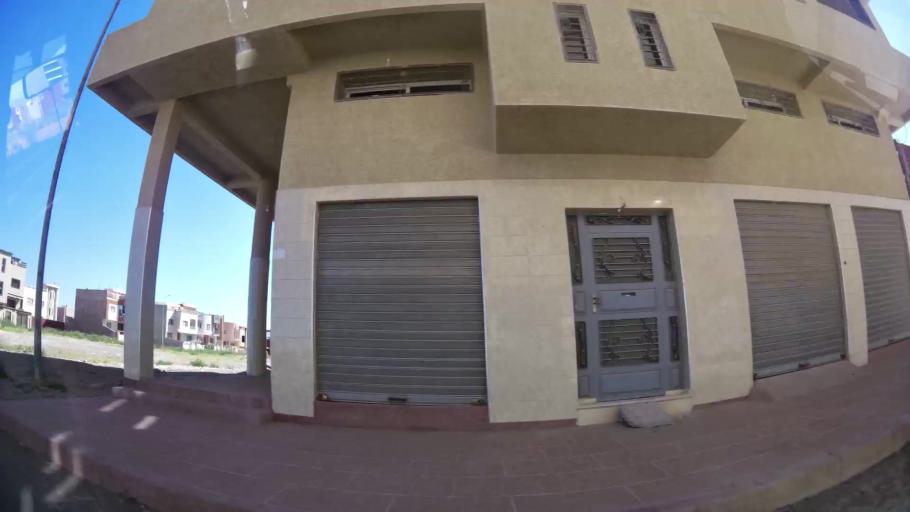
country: MA
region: Oriental
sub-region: Oujda-Angad
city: Oujda
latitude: 34.6528
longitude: -1.8858
